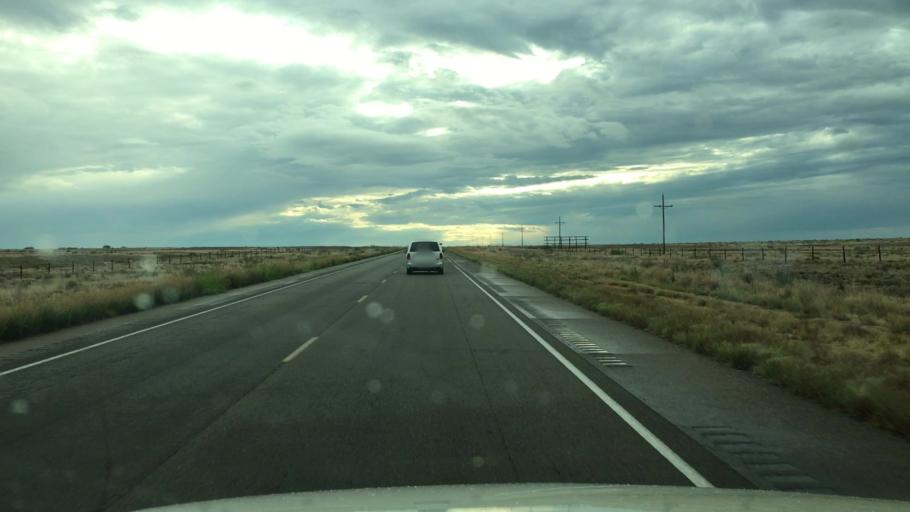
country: US
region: New Mexico
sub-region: Chaves County
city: Roswell
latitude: 33.4033
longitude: -104.3223
